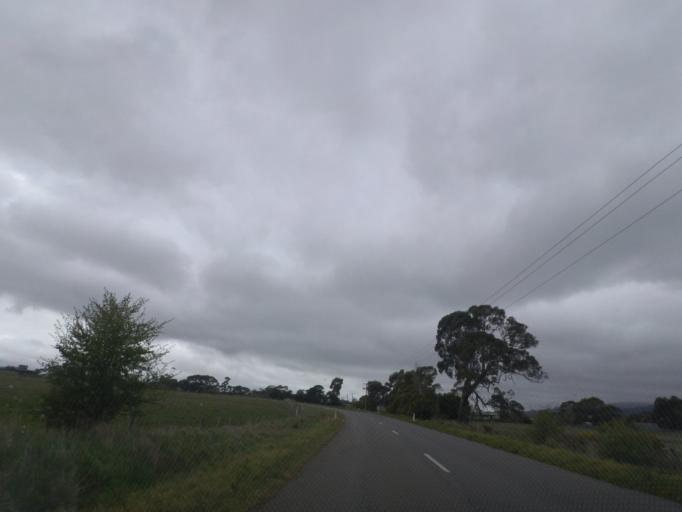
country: AU
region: Victoria
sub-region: Hume
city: Sunbury
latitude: -37.3250
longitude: 144.5566
